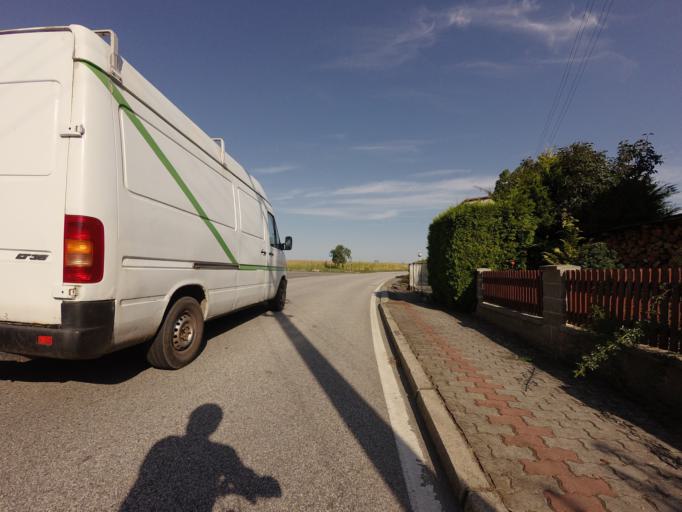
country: CZ
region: Jihocesky
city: Bernartice
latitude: 49.2985
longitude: 14.3857
